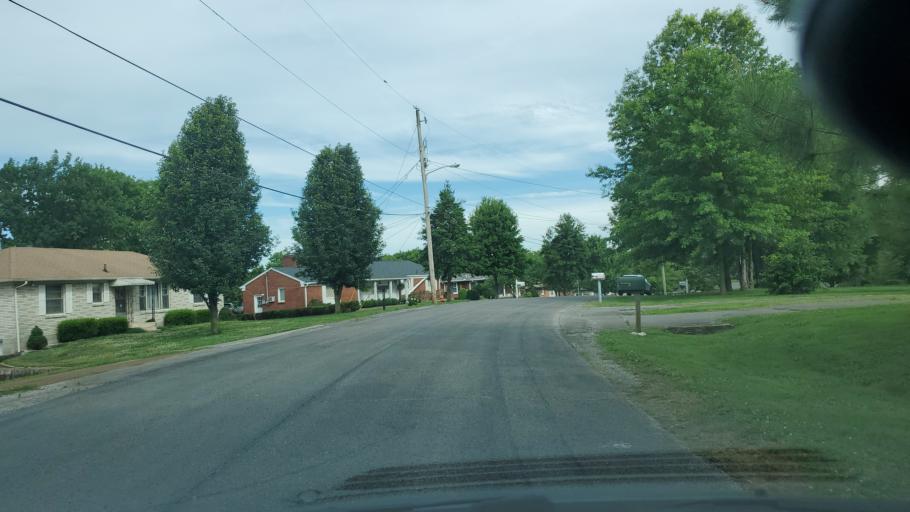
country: US
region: Tennessee
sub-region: Davidson County
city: Lakewood
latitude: 36.2111
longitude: -86.6821
